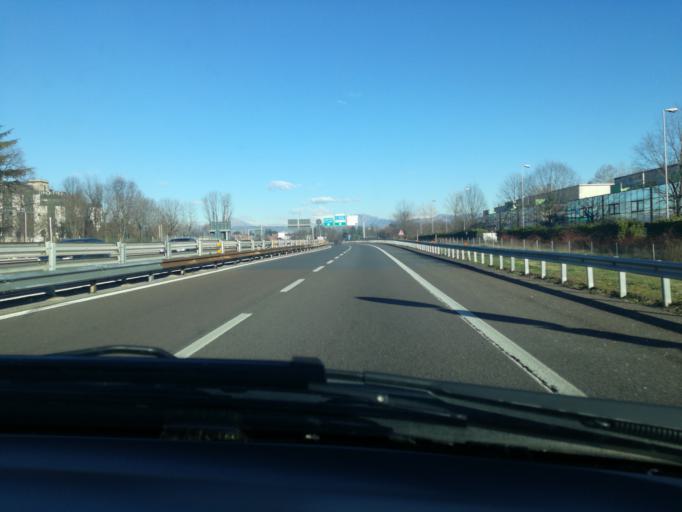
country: IT
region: Lombardy
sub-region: Provincia di Monza e Brianza
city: Vimercate
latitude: 45.5987
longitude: 9.3633
